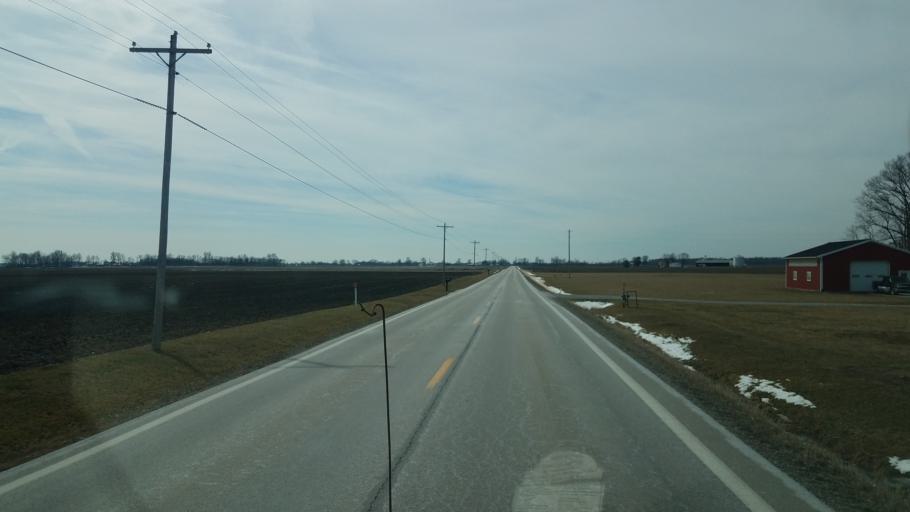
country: US
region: Ohio
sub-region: Delaware County
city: Delaware
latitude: 40.3184
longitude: -82.9906
